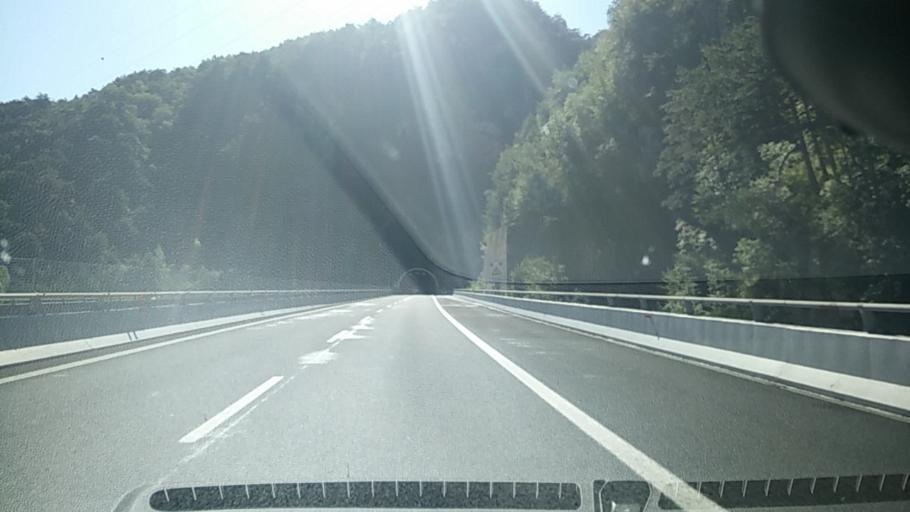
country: IT
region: Friuli Venezia Giulia
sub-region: Provincia di Udine
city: Moggio di Sotto
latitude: 46.3975
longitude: 13.1783
